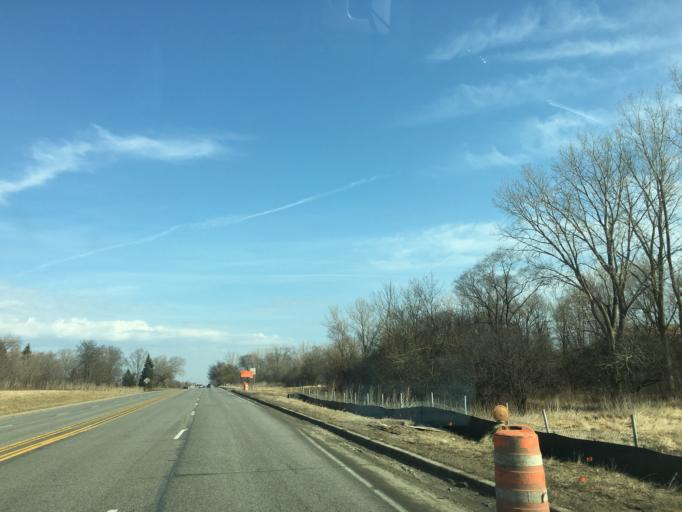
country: US
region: Illinois
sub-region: Cook County
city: Hoffman Estates
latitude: 42.0705
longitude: -88.0779
